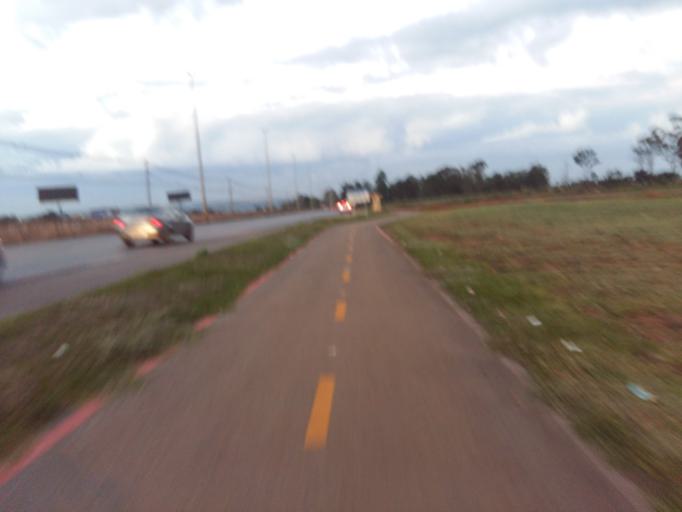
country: BR
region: Federal District
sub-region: Brasilia
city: Brasilia
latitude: -15.6867
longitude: -47.8579
